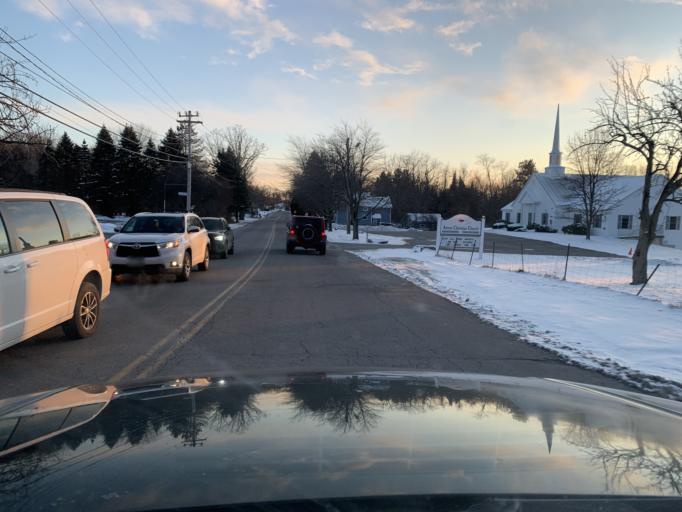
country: US
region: Massachusetts
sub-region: Essex County
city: Haverhill
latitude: 42.7821
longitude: -71.1117
